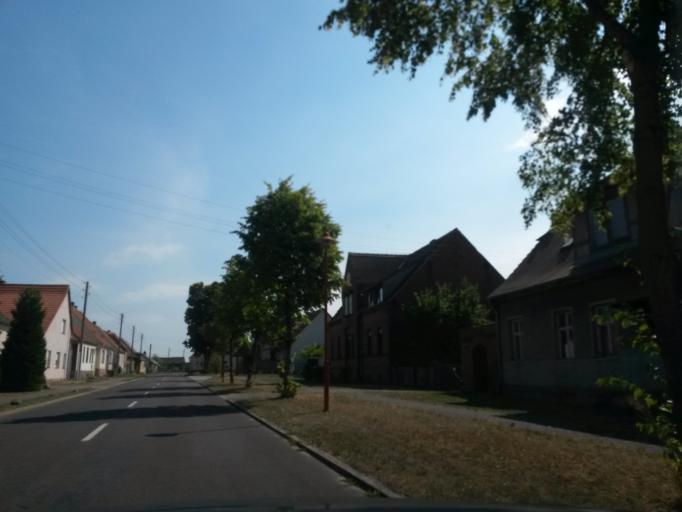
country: DE
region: Saxony-Anhalt
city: Klieken
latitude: 52.0084
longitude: 12.3760
